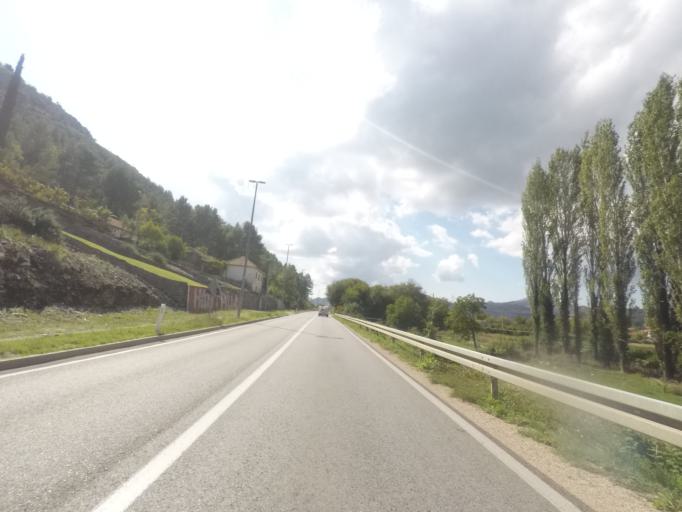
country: BA
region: Republika Srpska
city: Trebinje
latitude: 42.6934
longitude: 18.3394
